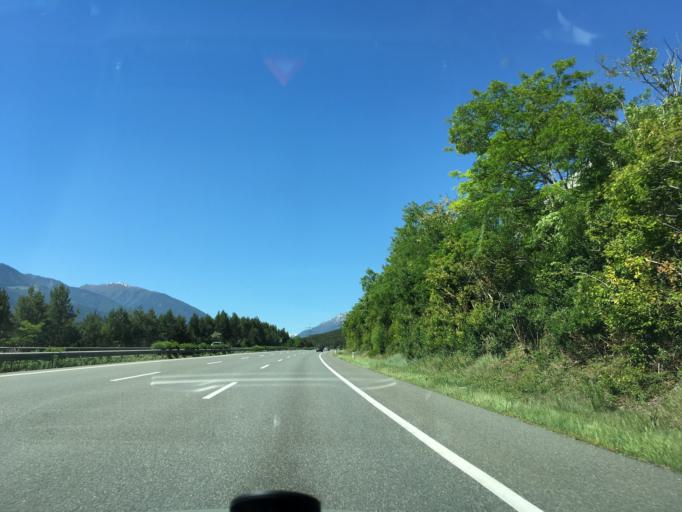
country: AT
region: Tyrol
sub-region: Politischer Bezirk Imst
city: Haiming
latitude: 47.2551
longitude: 10.8666
